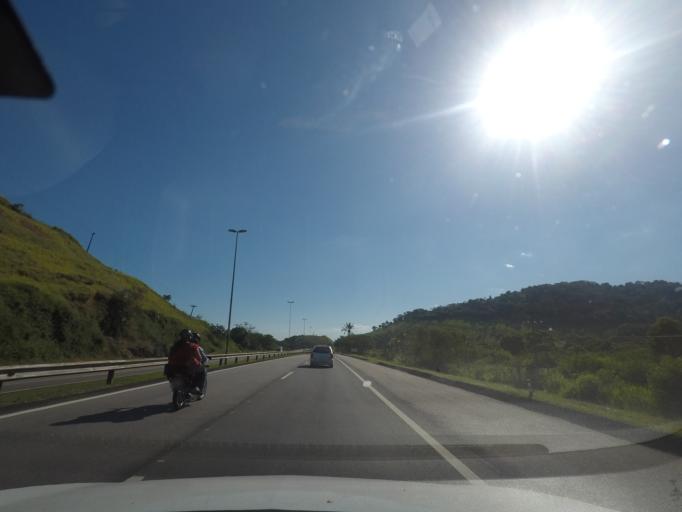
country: BR
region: Rio de Janeiro
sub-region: Guapimirim
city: Guapimirim
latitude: -22.6308
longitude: -43.0516
